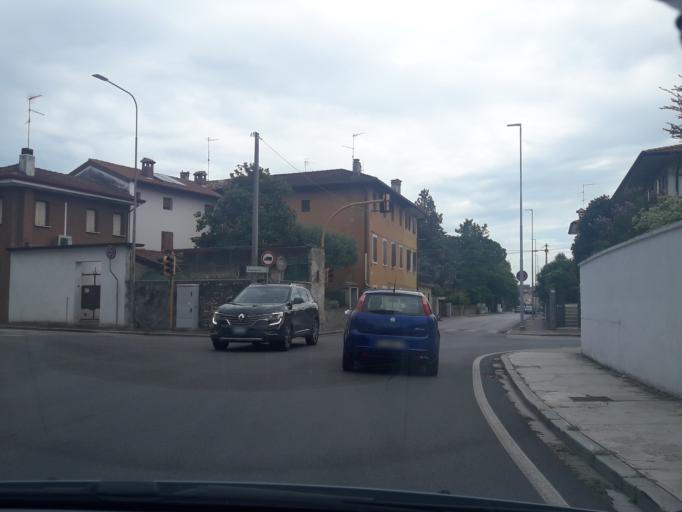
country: IT
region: Friuli Venezia Giulia
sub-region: Provincia di Udine
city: Feletto Umberto
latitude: 46.0866
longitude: 13.2308
